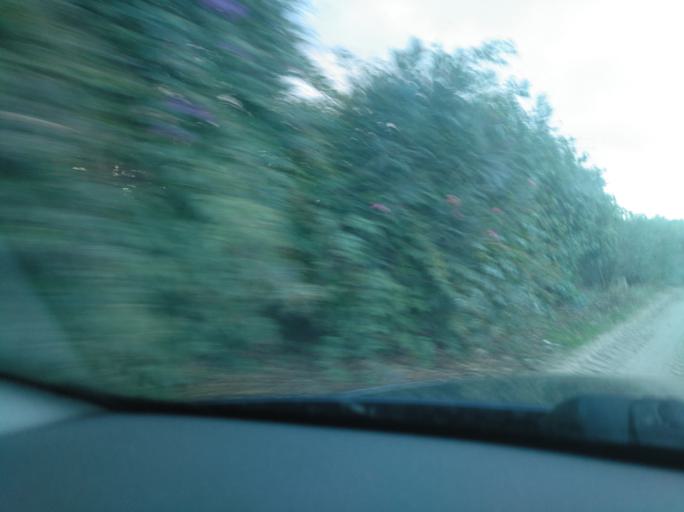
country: PT
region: Portalegre
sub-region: Campo Maior
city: Campo Maior
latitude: 39.0124
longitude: -7.0516
